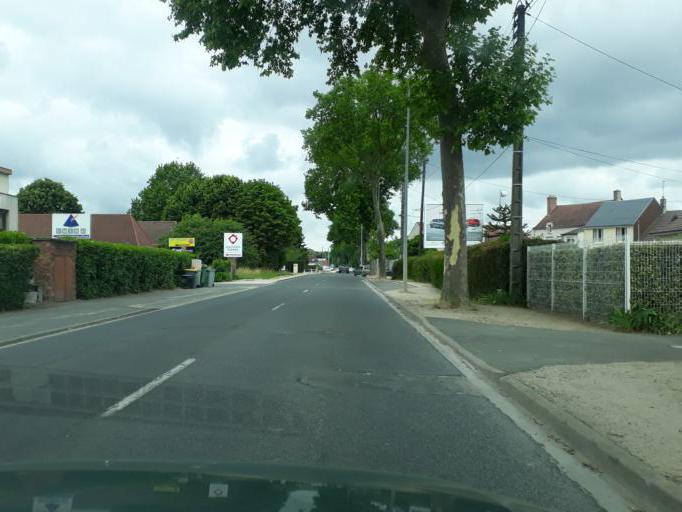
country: FR
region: Centre
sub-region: Departement du Loiret
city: Saint-Denis-en-Val
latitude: 47.8762
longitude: 1.9419
